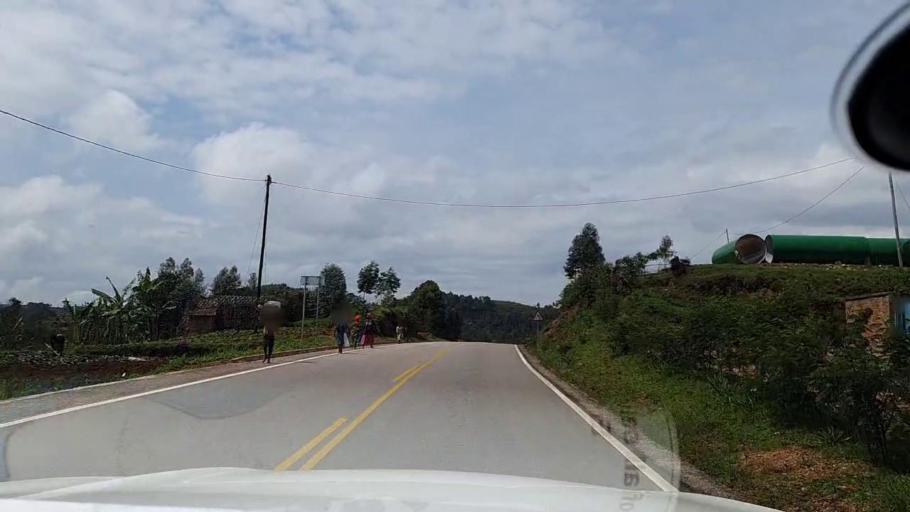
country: RW
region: Southern Province
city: Nzega
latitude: -2.4876
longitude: 29.5130
